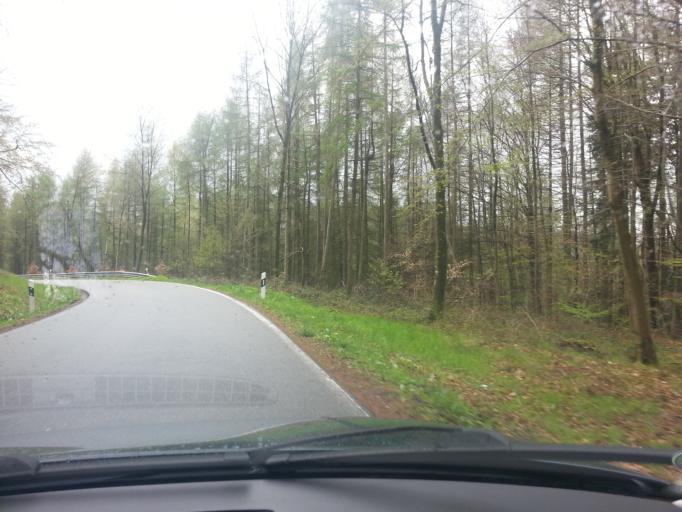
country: DE
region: Rheinland-Pfalz
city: Kashofen
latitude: 49.3199
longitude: 7.4006
